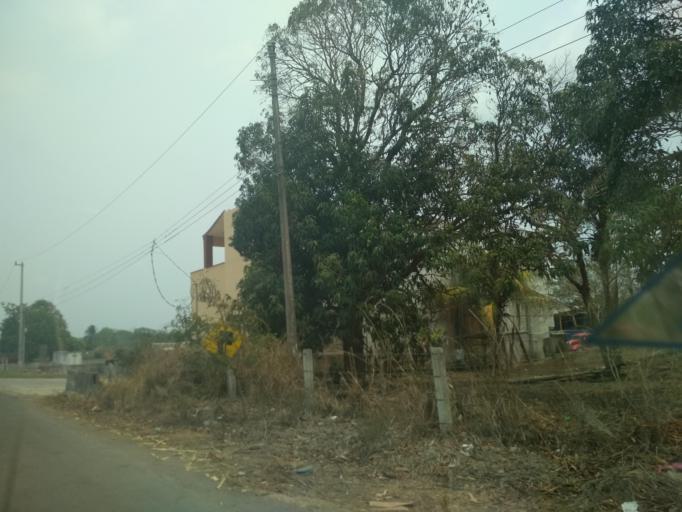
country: MX
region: Veracruz
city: Paso del Toro
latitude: 19.0332
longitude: -96.1486
